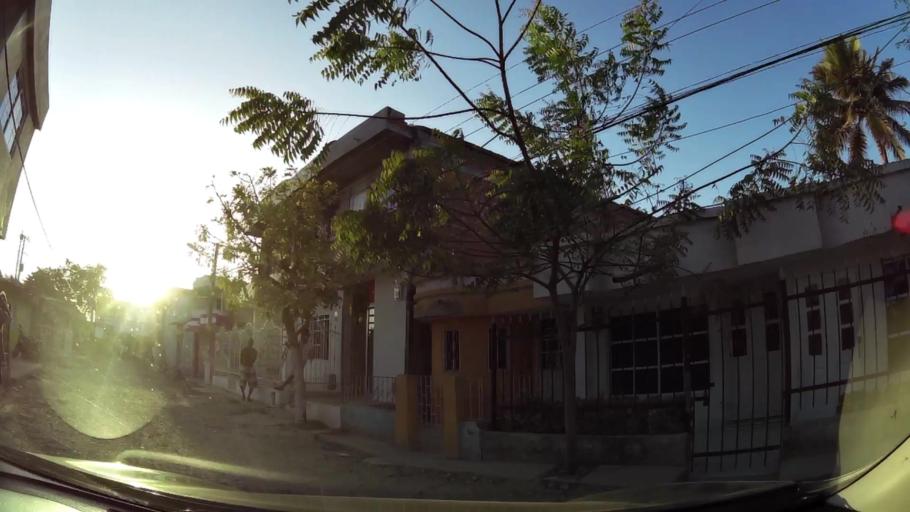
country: CO
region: Bolivar
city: Cartagena
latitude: 10.4121
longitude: -75.4566
